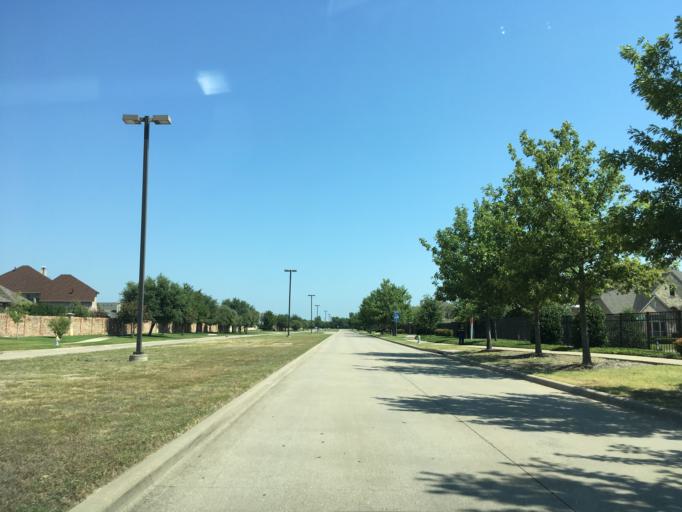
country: US
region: Texas
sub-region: Collin County
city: Allen
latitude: 33.1347
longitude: -96.6763
